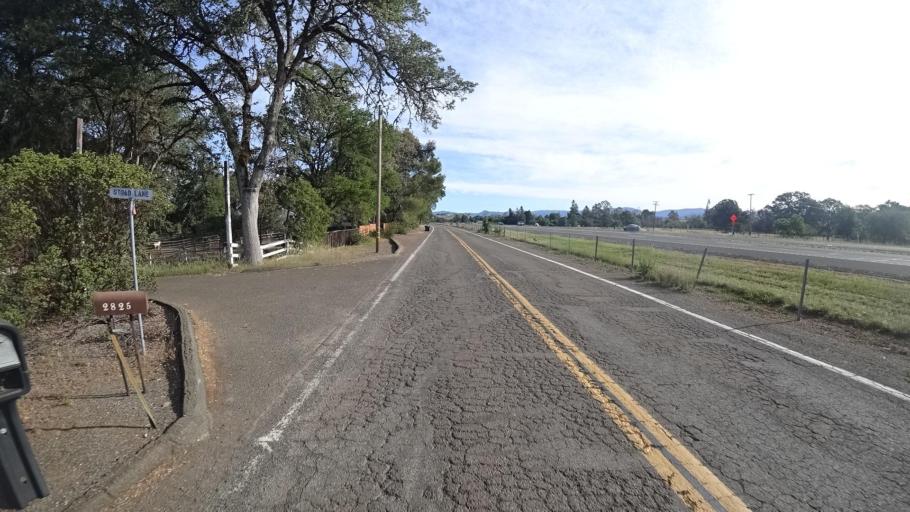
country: US
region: California
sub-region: Lake County
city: North Lakeport
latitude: 39.0725
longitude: -122.9315
